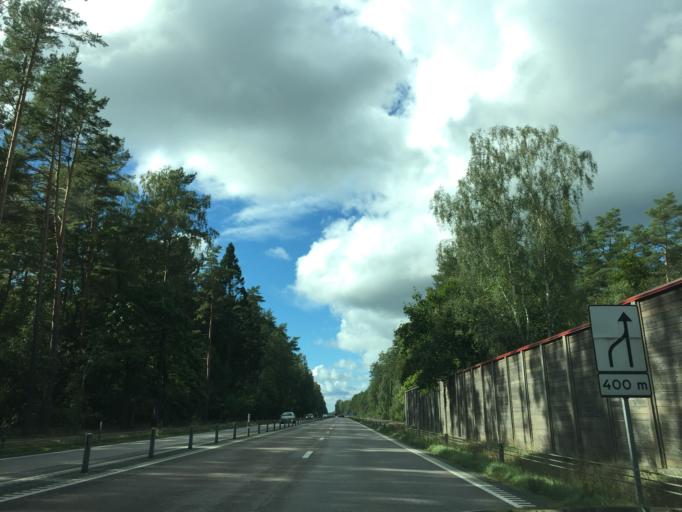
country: SE
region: Skane
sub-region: Sjobo Kommun
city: Sjoebo
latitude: 55.6367
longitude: 13.6640
